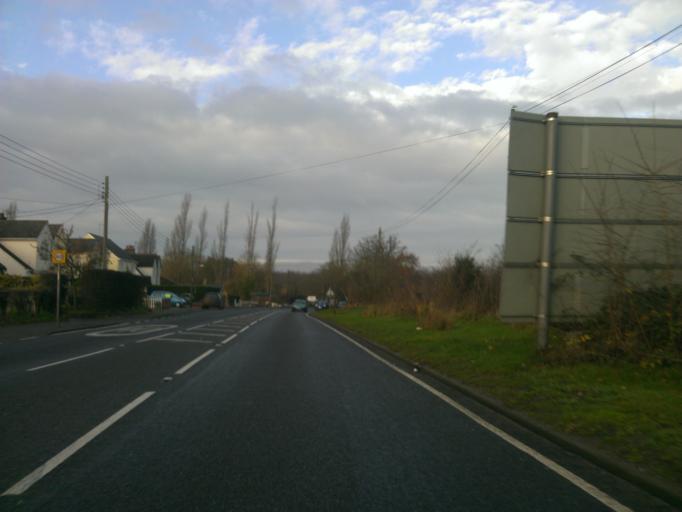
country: GB
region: England
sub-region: Essex
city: Alresford
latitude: 51.8427
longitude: 1.0274
